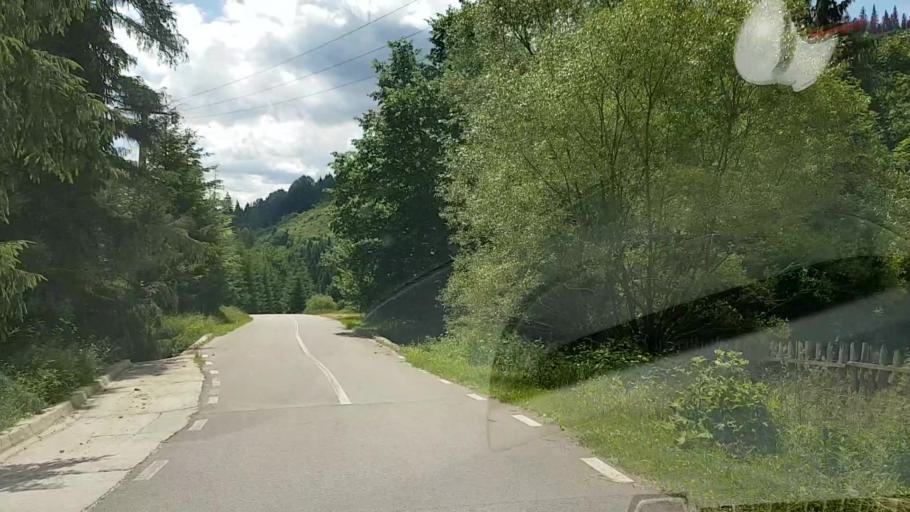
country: RO
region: Suceava
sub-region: Comuna Crucea
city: Crucea
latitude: 47.4238
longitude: 25.5792
